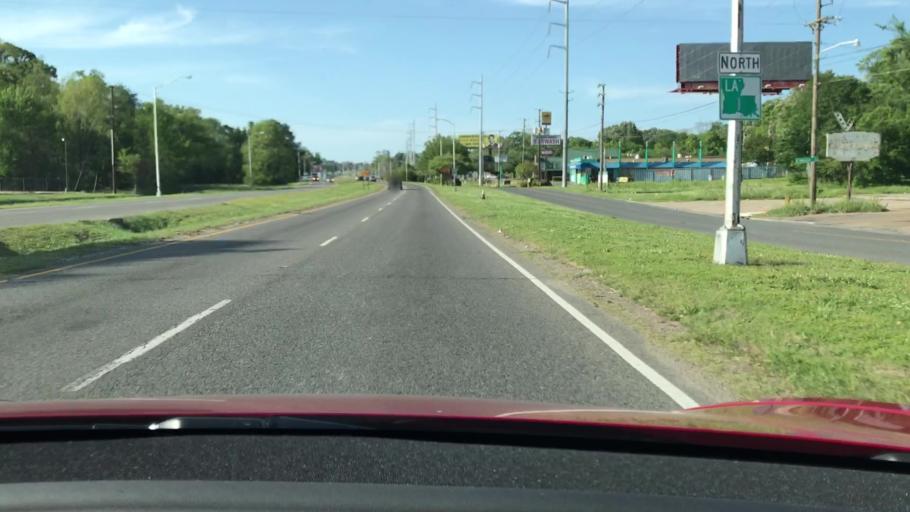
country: US
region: Louisiana
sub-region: Bossier Parish
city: Bossier City
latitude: 32.4851
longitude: -93.7240
